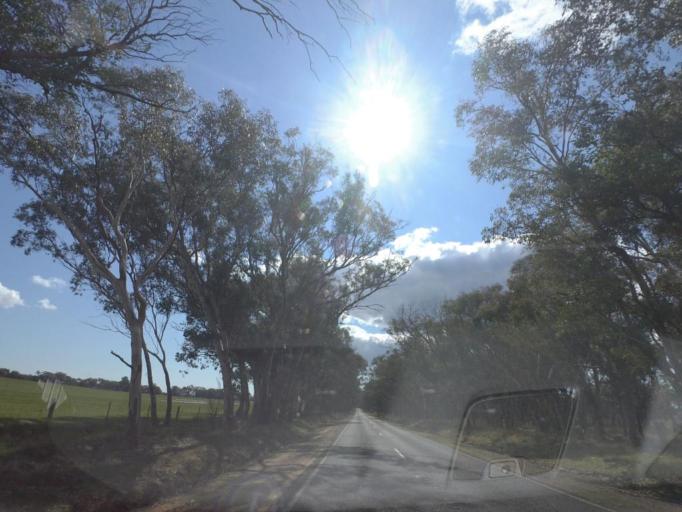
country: AU
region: New South Wales
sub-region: Corowa Shire
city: Howlong
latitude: -36.2272
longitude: 146.6297
